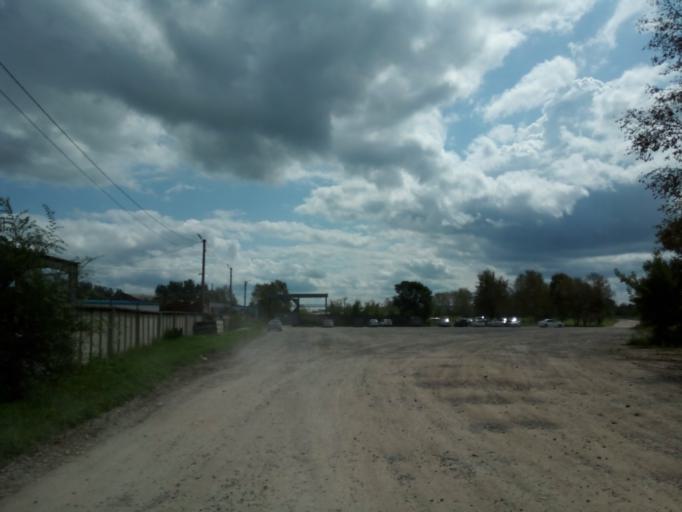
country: RU
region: Primorskiy
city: Dal'nerechensk
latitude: 45.9510
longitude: 133.8237
